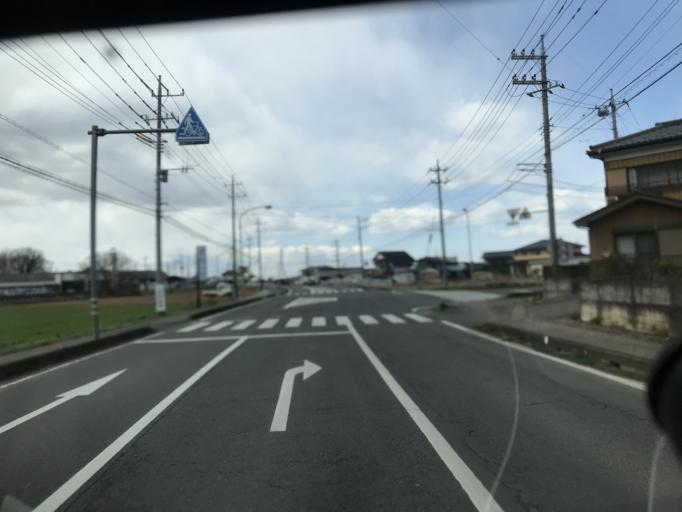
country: JP
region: Ibaraki
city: Shimodate
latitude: 36.2479
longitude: 139.9373
